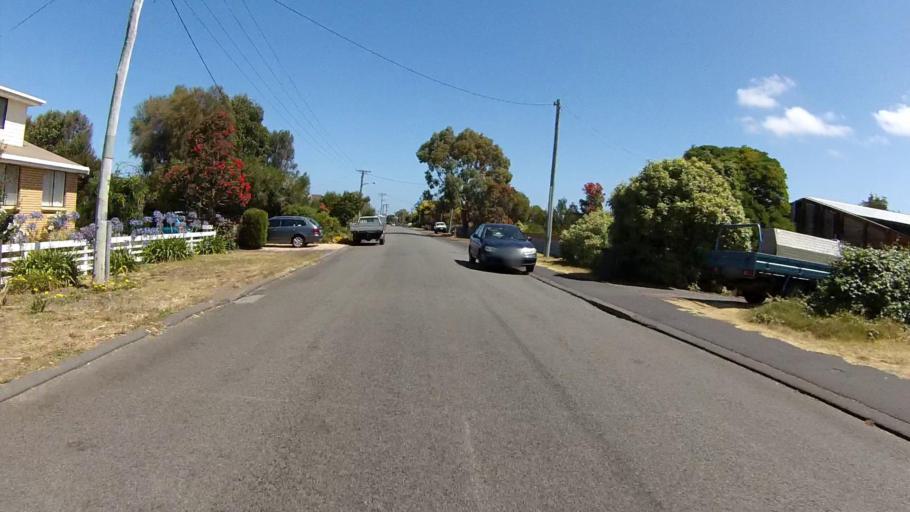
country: AU
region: Tasmania
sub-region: Clarence
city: Lauderdale
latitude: -42.8995
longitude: 147.4964
